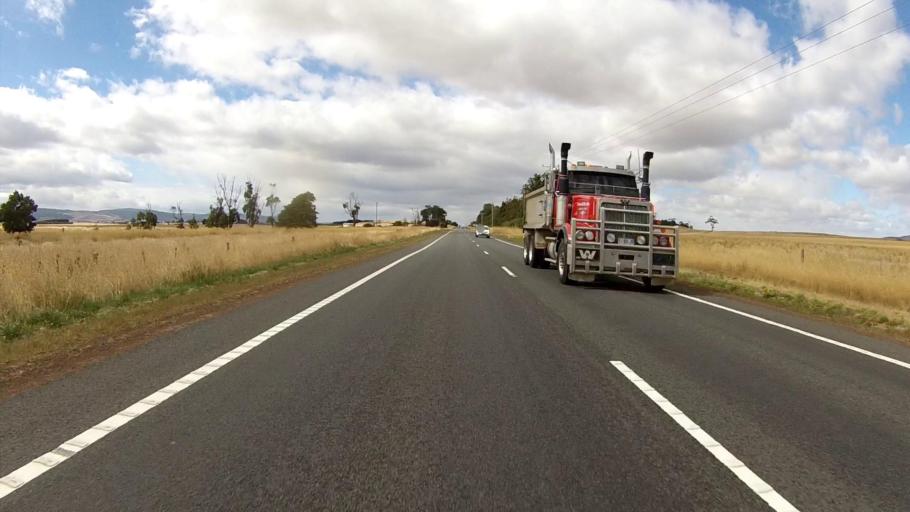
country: AU
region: Tasmania
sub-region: Northern Midlands
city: Evandale
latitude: -41.8994
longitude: 147.4754
